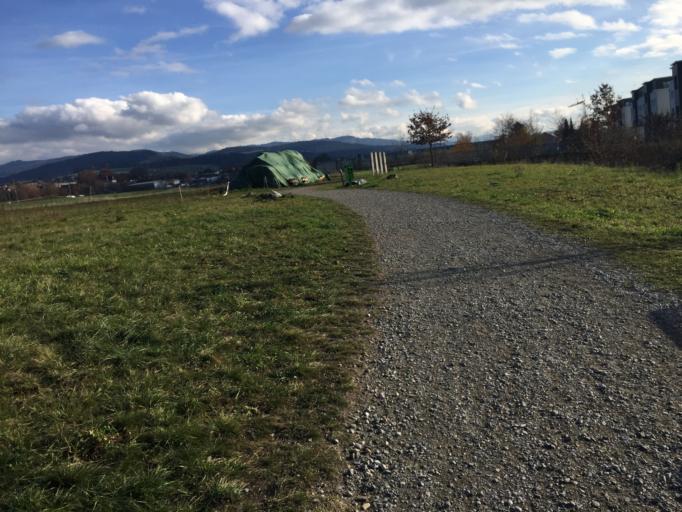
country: CH
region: Bern
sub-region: Bern-Mittelland District
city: Munsingen
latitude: 46.8780
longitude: 7.5492
